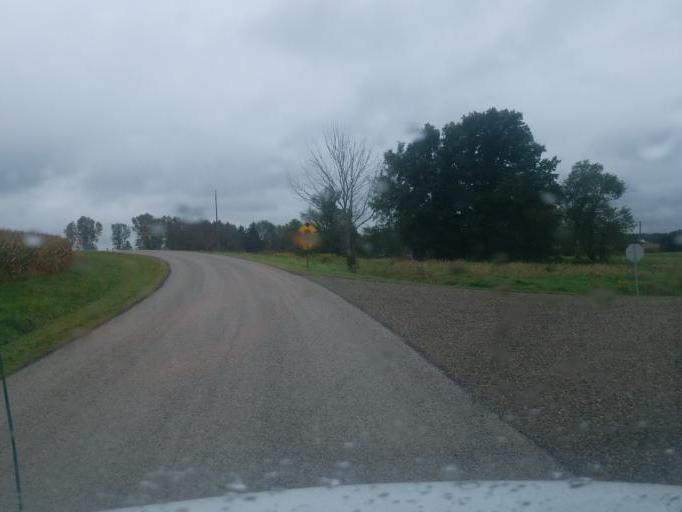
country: US
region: Ohio
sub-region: Ashland County
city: Ashland
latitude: 40.7863
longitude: -82.2072
